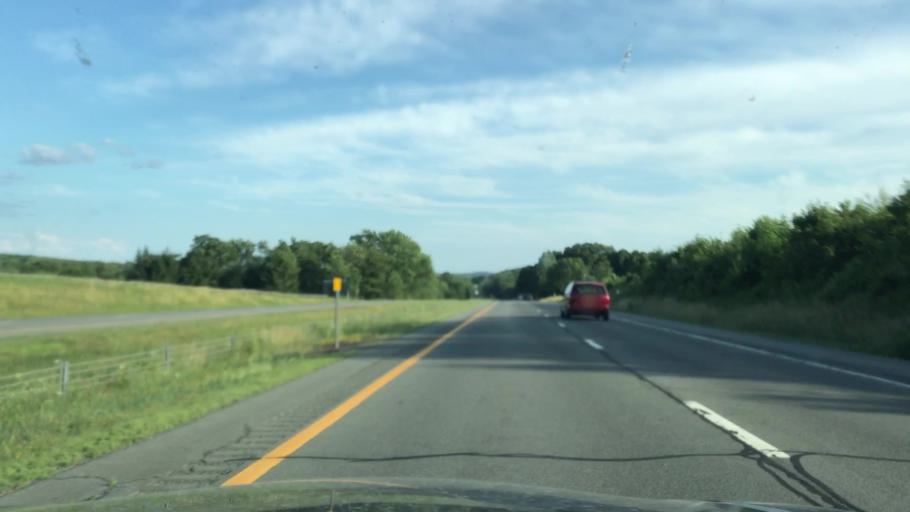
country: US
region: New York
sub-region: Sullivan County
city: Liberty
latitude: 41.7512
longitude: -74.7343
